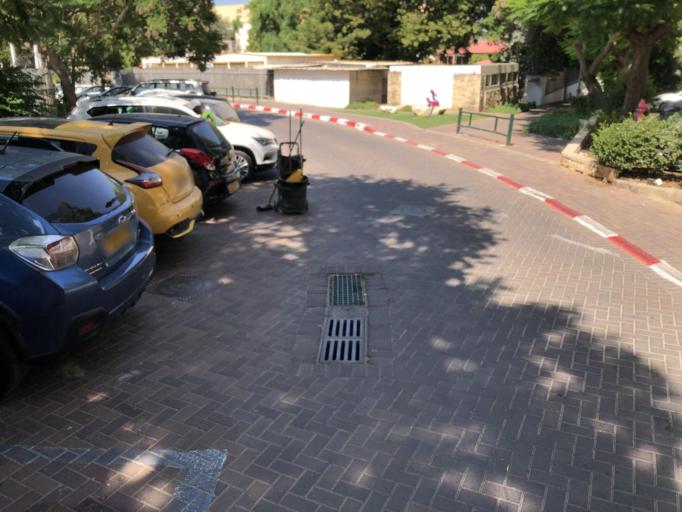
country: IL
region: Central District
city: Yehud
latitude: 32.0340
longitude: 34.8790
